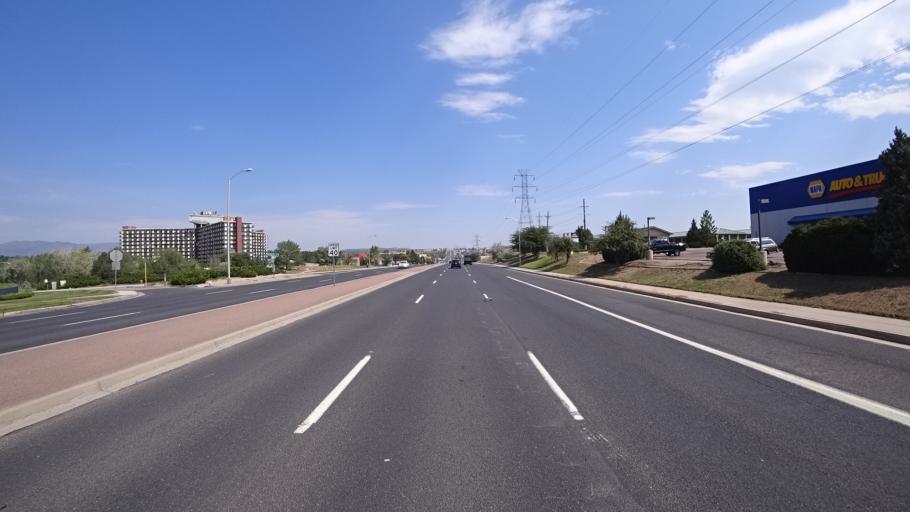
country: US
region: Colorado
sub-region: El Paso County
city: Stratmoor
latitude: 38.8206
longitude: -104.7574
